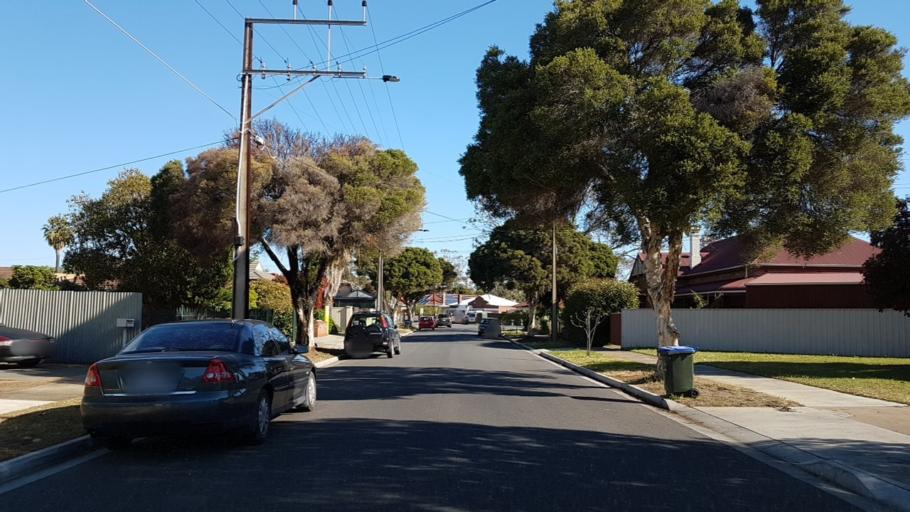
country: AU
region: South Australia
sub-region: Charles Sturt
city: Woodville North
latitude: -34.8706
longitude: 138.5423
